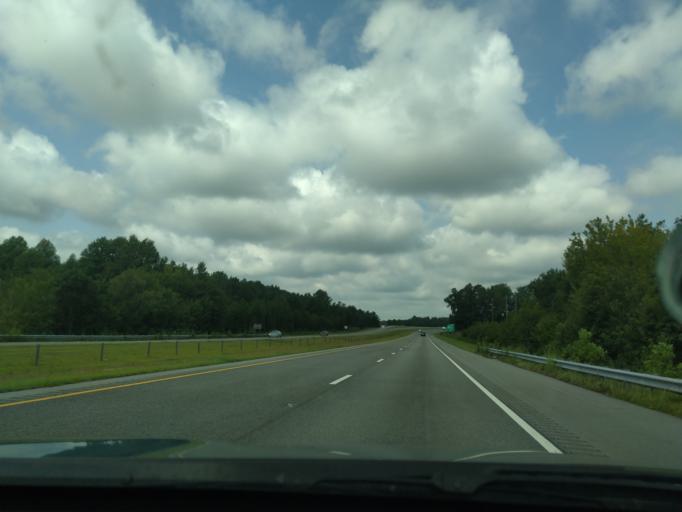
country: US
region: North Carolina
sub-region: Martin County
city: Robersonville
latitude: 35.8273
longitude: -77.1736
